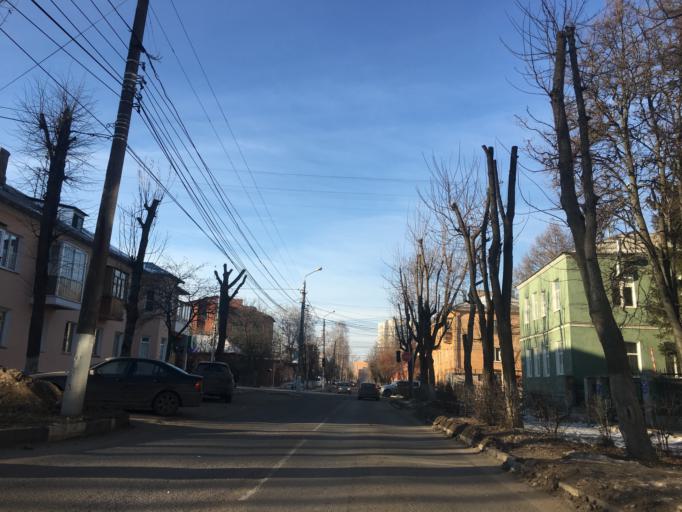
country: RU
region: Tula
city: Mendeleyevskiy
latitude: 54.1713
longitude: 37.5863
